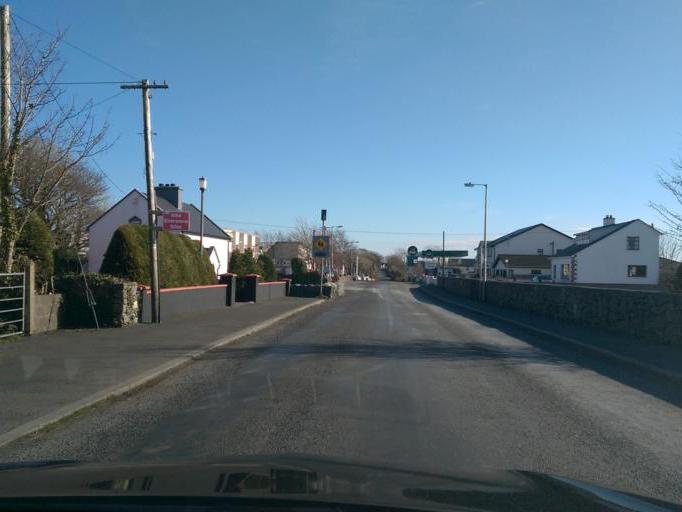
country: IE
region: Connaught
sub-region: County Galway
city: Oranmore
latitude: 53.2329
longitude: -8.9506
